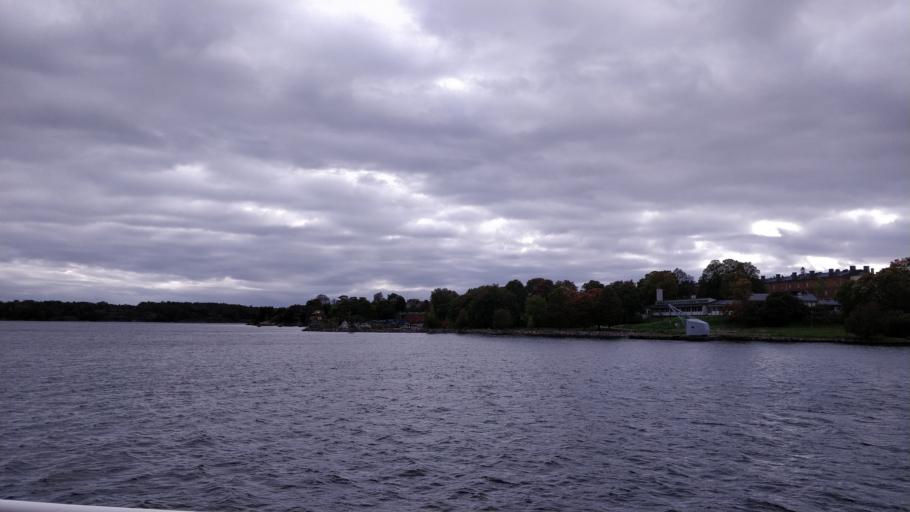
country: FI
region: Uusimaa
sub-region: Helsinki
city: Helsinki
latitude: 60.1506
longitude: 24.9916
